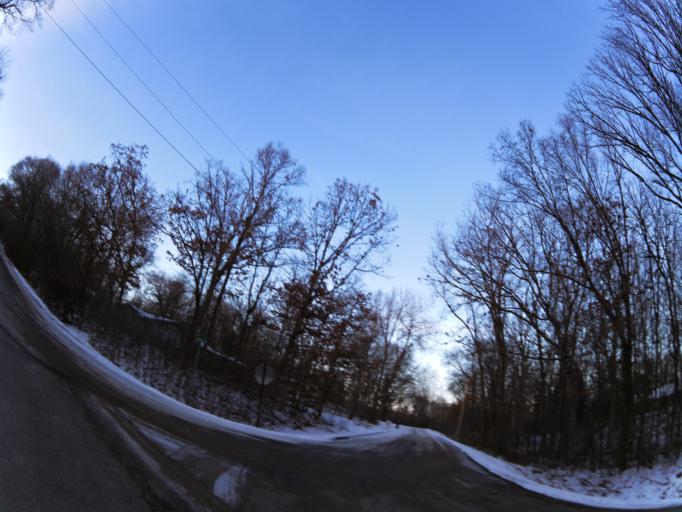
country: US
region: Minnesota
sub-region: Washington County
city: Lake Elmo
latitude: 44.9667
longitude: -92.8370
